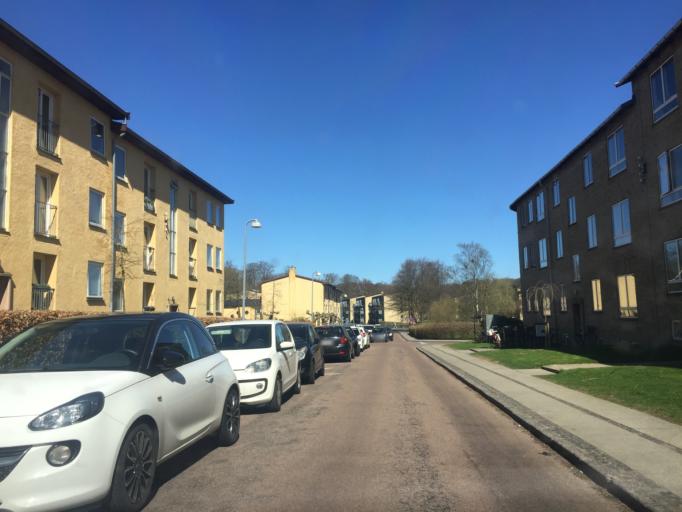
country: DK
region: Capital Region
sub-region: Rudersdal Kommune
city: Holte
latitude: 55.7953
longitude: 12.4801
